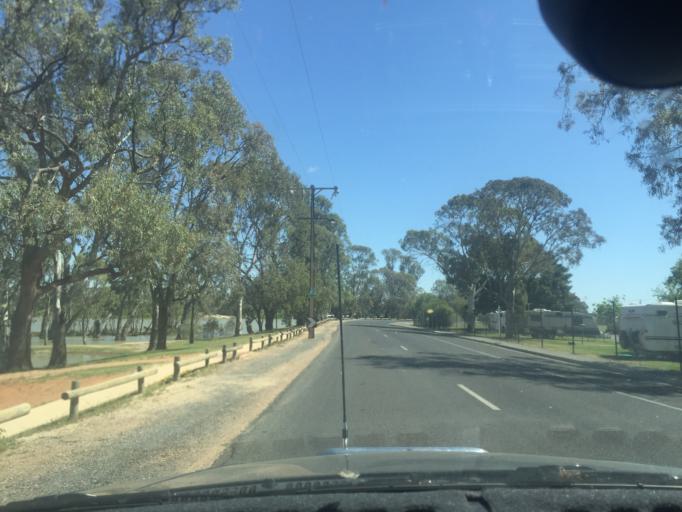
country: AU
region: South Australia
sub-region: Berri and Barmera
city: Berri
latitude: -34.2870
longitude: 140.6095
